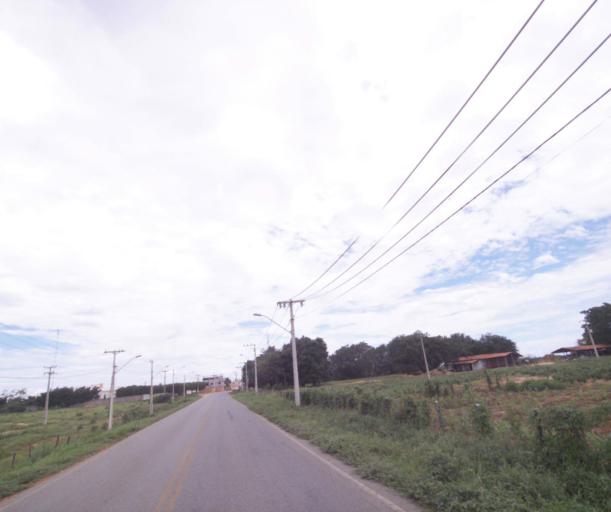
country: BR
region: Bahia
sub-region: Carinhanha
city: Carinhanha
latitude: -14.3319
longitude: -43.7693
